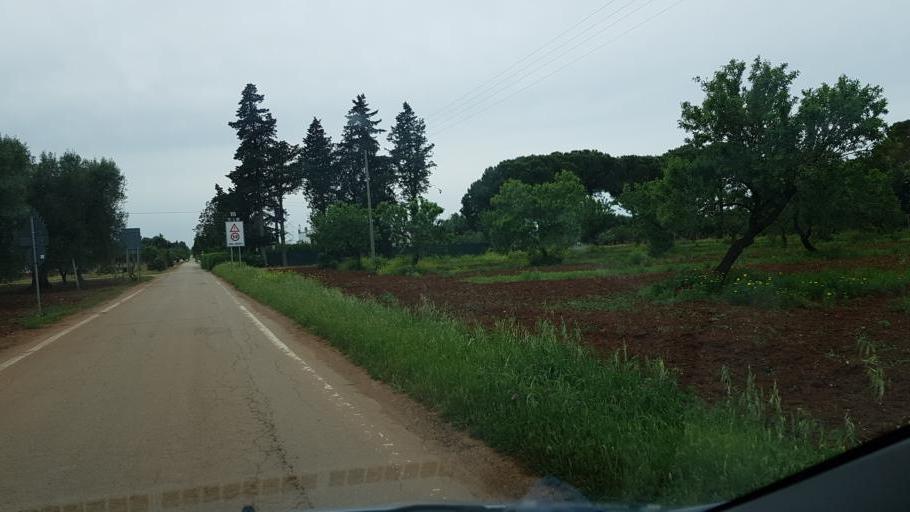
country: IT
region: Apulia
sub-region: Provincia di Brindisi
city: San Vito dei Normanni
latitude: 40.6652
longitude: 17.7770
